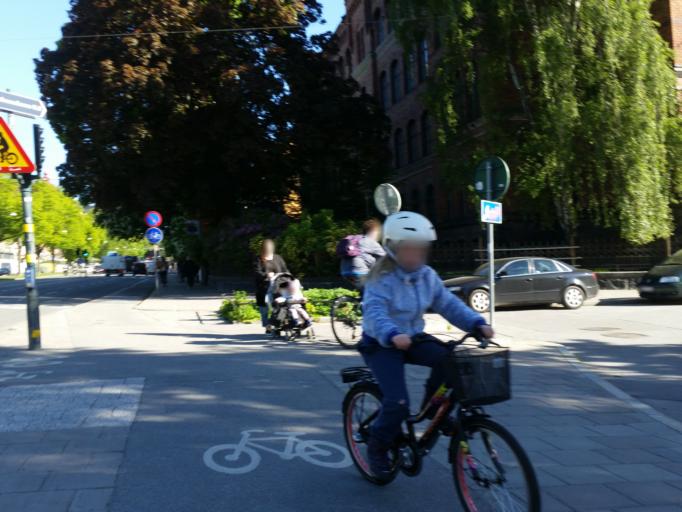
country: SE
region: Stockholm
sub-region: Stockholms Kommun
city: Arsta
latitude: 59.3145
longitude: 18.0523
